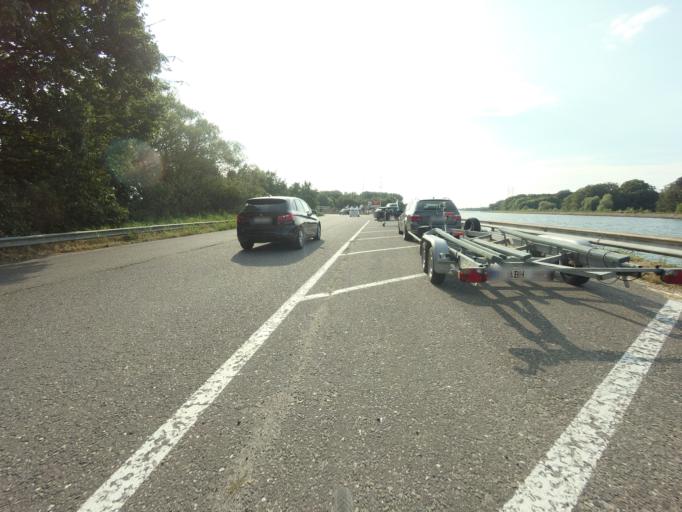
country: BE
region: Flanders
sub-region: Provincie Antwerpen
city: Zandhoven
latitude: 51.1969
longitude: 4.6314
